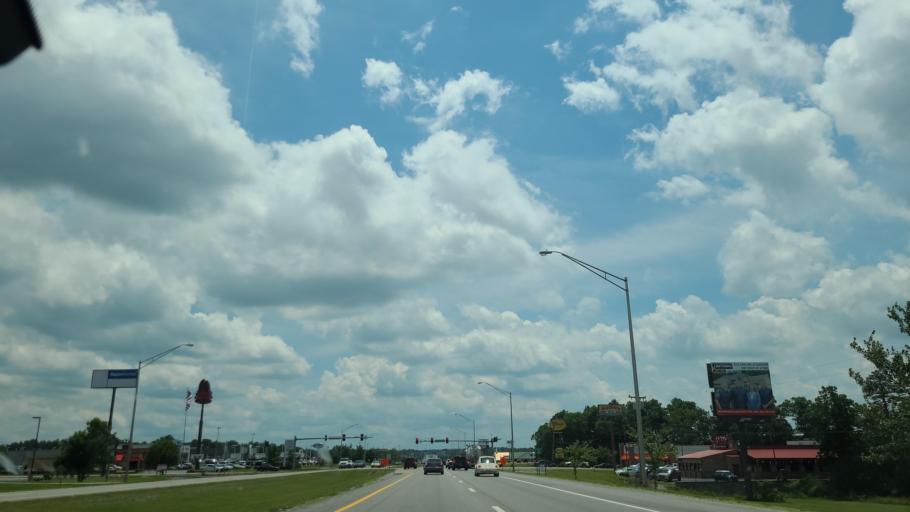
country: US
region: Tennessee
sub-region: Cumberland County
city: Crossville
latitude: 35.9881
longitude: -85.0391
